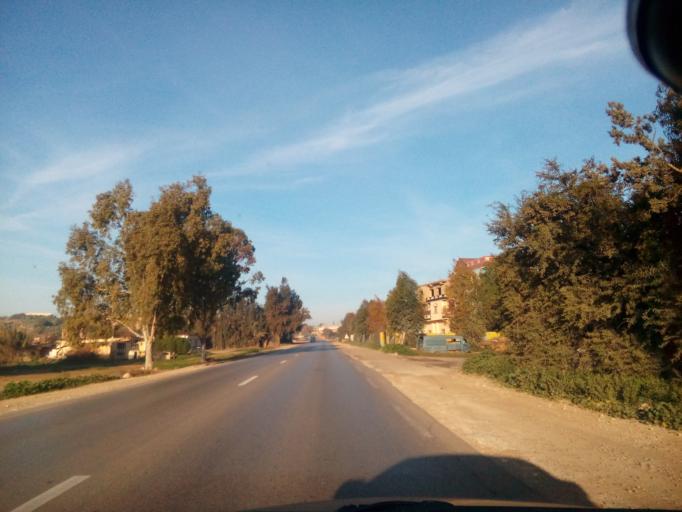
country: DZ
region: Relizane
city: Relizane
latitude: 35.7179
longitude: 0.3308
